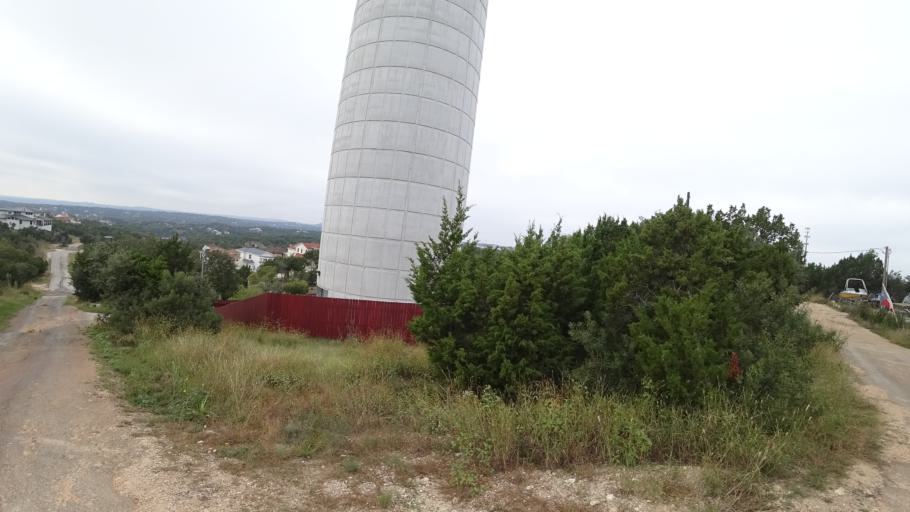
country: US
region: Texas
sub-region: Travis County
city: Hudson Bend
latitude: 30.3950
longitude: -97.9212
